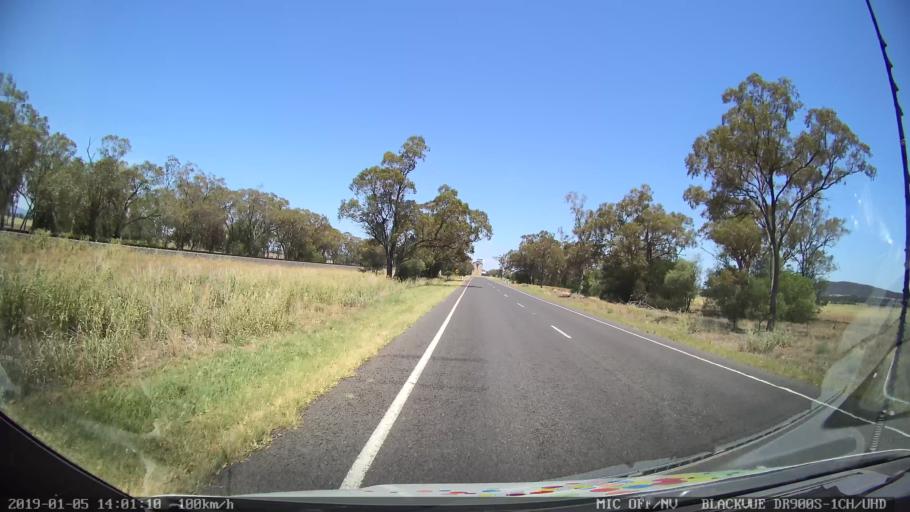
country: AU
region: New South Wales
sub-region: Gunnedah
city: Gunnedah
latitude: -31.1669
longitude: 150.3216
